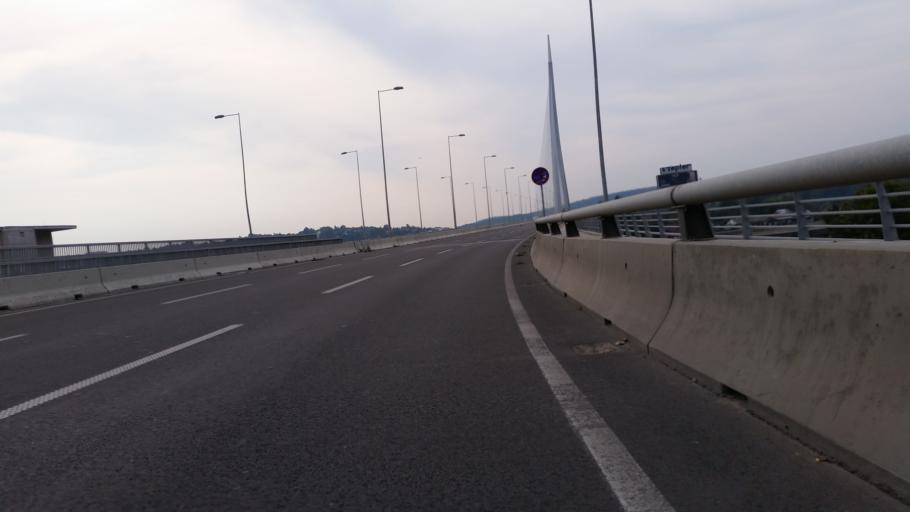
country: RS
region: Central Serbia
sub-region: Belgrade
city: Novi Beograd
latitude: 44.8017
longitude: 20.4245
